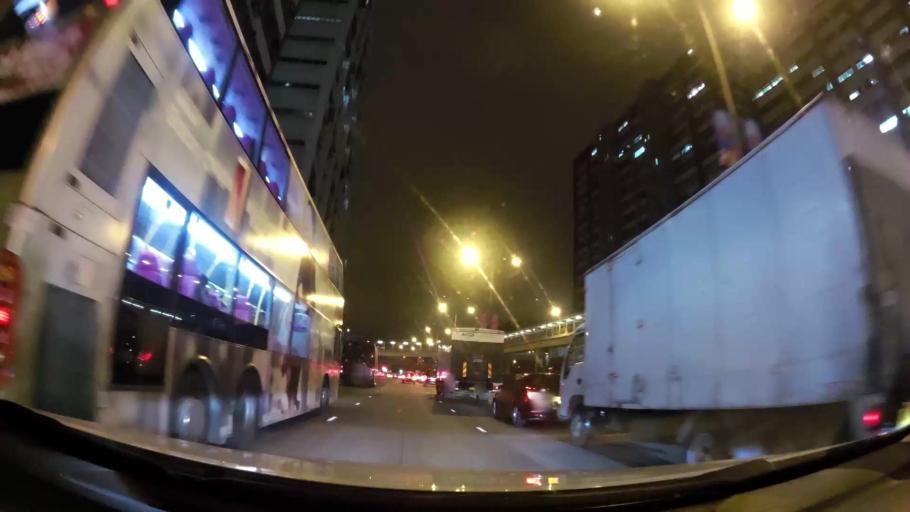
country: HK
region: Tsuen Wan
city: Tsuen Wan
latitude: 22.3568
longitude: 114.1248
